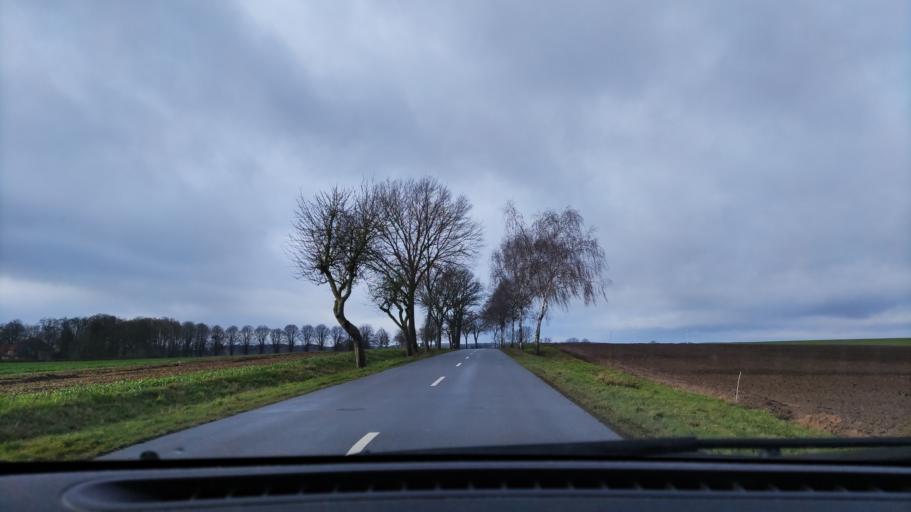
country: DE
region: Lower Saxony
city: Natendorf
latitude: 53.0811
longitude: 10.4925
